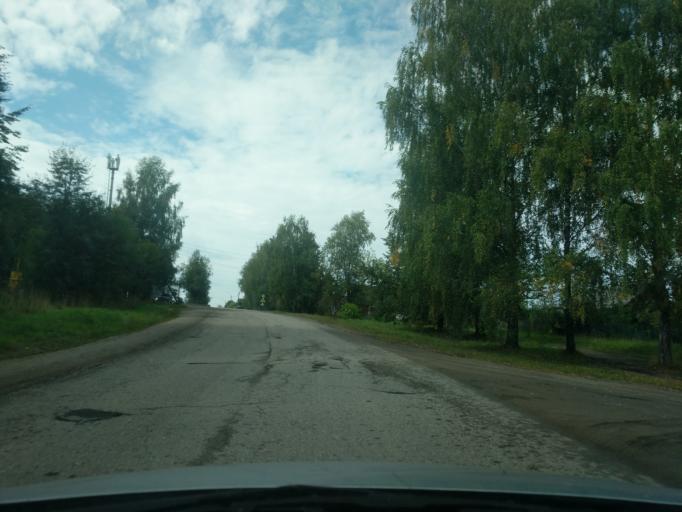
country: RU
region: Kostroma
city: Sudislavl'
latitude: 57.8807
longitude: 41.7190
